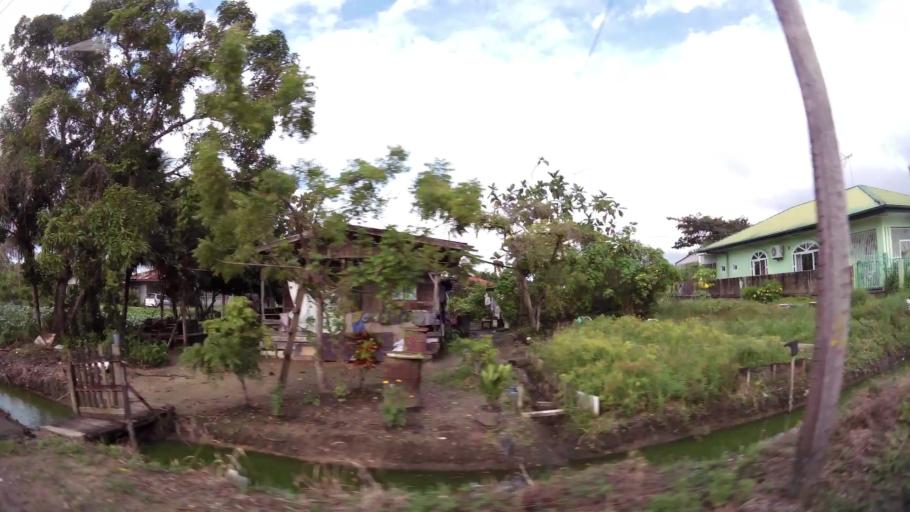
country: SR
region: Paramaribo
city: Paramaribo
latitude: 5.8452
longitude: -55.2641
